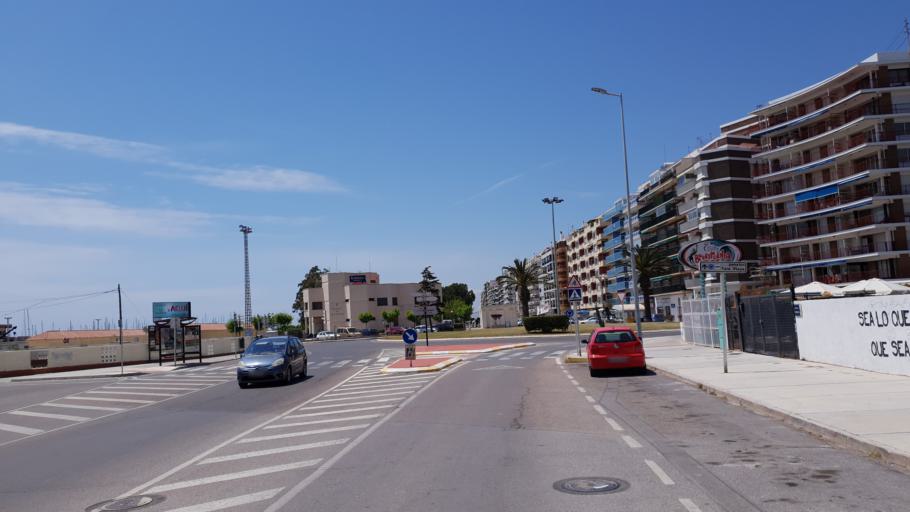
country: ES
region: Valencia
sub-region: Provincia de Castello
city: Burriana
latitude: 39.8662
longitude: -0.0711
